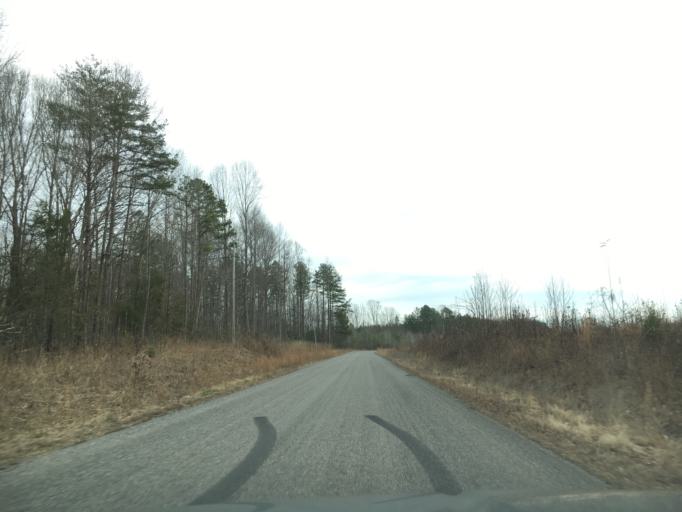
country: US
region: Virginia
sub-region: Amelia County
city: Amelia Court House
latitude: 37.4240
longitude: -77.9955
